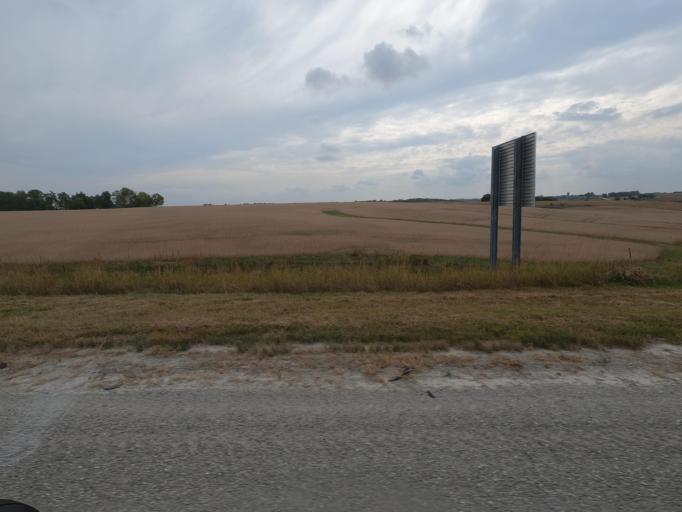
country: US
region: Iowa
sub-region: Jasper County
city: Monroe
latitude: 41.5112
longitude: -93.1181
